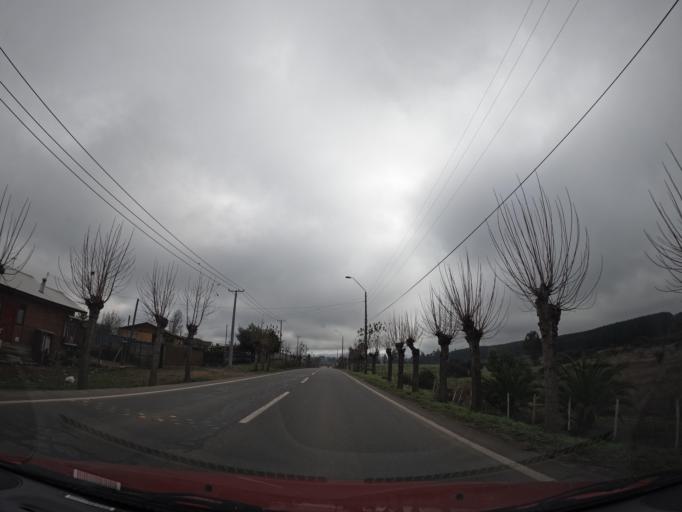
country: CL
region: Maule
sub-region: Provincia de Cauquenes
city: Cauquenes
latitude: -36.2725
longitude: -72.5433
